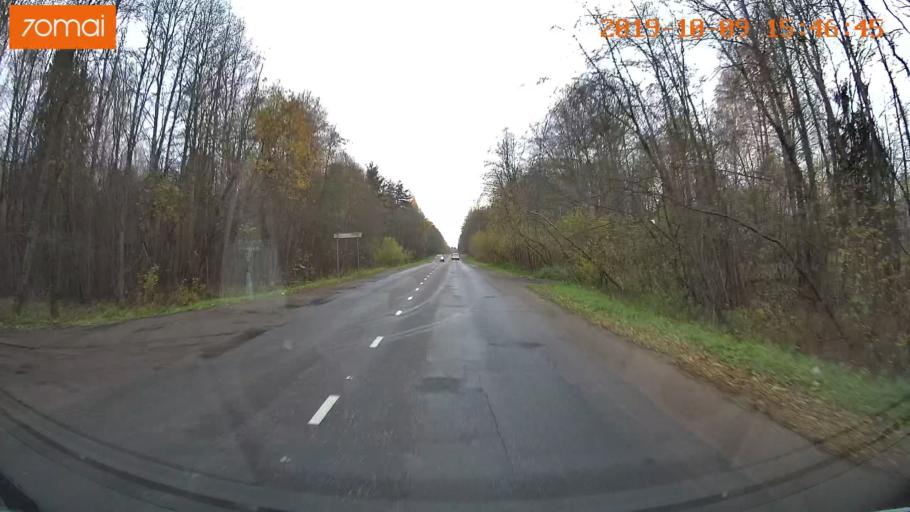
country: RU
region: Kostroma
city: Oktyabr'skiy
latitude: 57.8224
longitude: 41.0390
